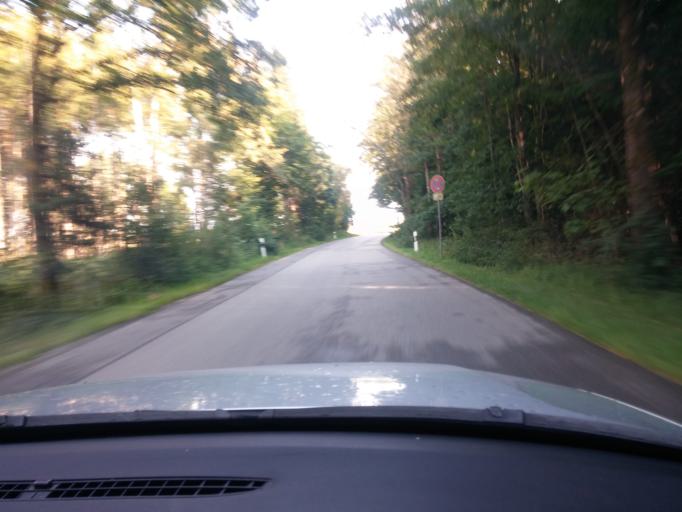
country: DE
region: Bavaria
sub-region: Upper Bavaria
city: Grasbrunn
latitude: 48.0908
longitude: 11.7354
